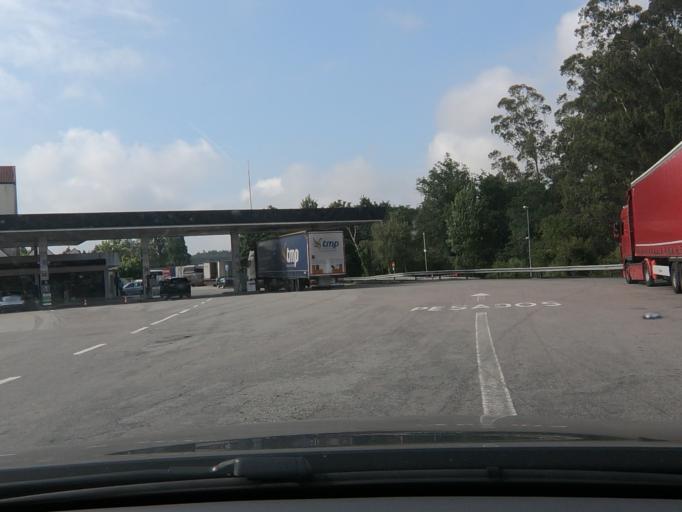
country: PT
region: Aveiro
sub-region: Estarreja
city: Beduido
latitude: 40.7564
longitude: -8.5372
